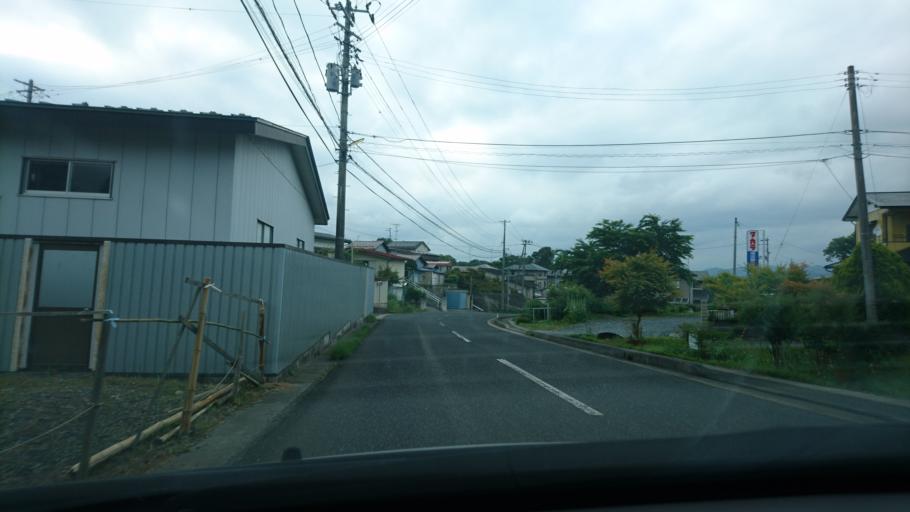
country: JP
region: Iwate
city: Ichinoseki
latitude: 38.9078
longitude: 141.1539
